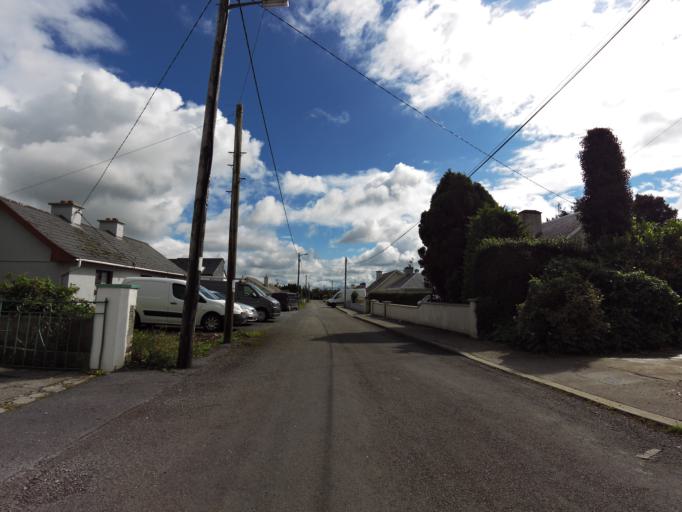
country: IE
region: Connaught
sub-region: County Galway
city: Loughrea
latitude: 53.2065
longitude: -8.5737
